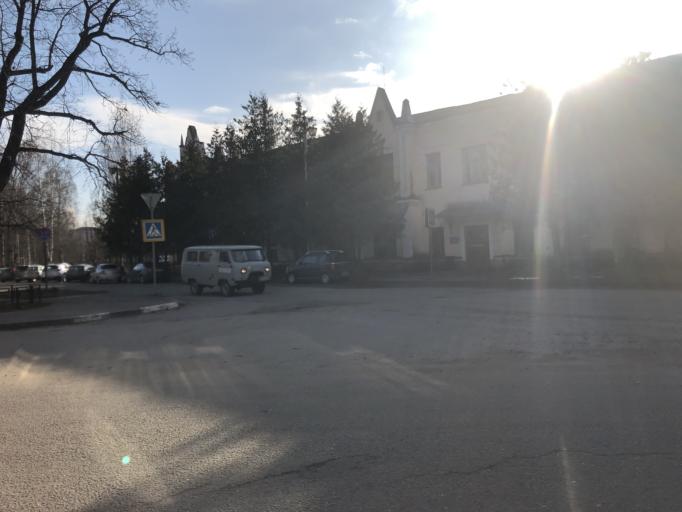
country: RU
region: Tverskaya
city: Rzhev
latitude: 56.2584
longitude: 34.3343
